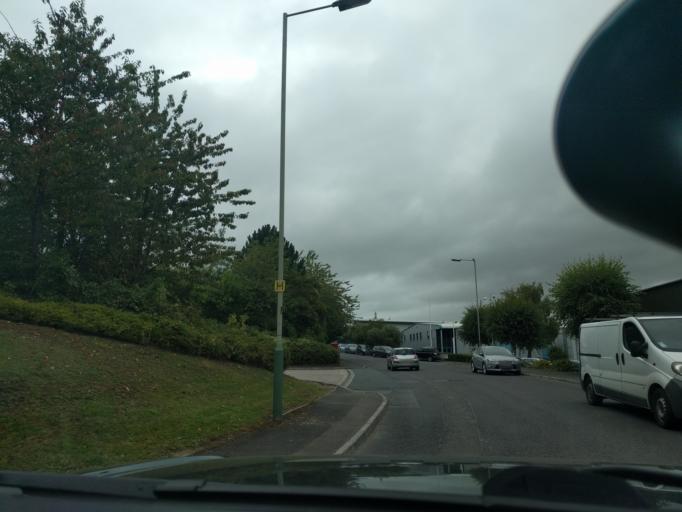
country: GB
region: England
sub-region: Wiltshire
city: Neston
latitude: 51.4207
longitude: -2.1989
